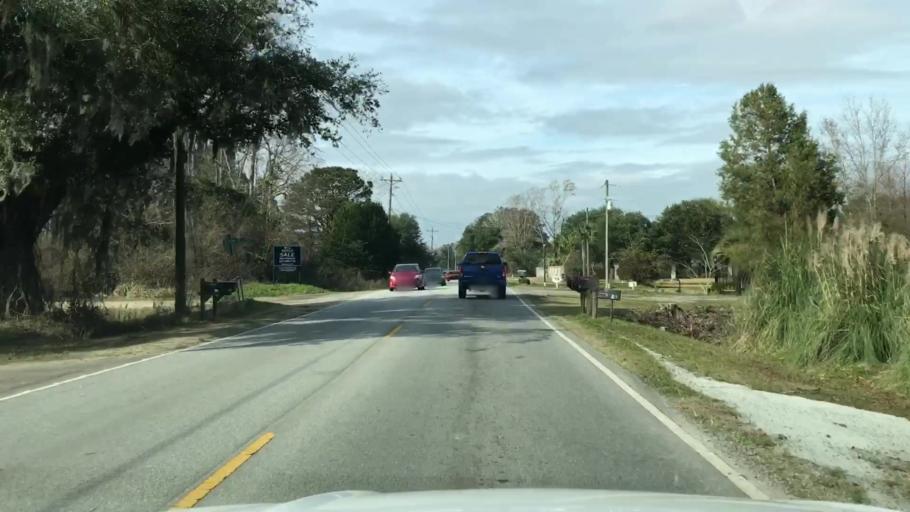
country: US
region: South Carolina
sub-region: Charleston County
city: Shell Point
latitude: 32.7715
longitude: -80.0797
